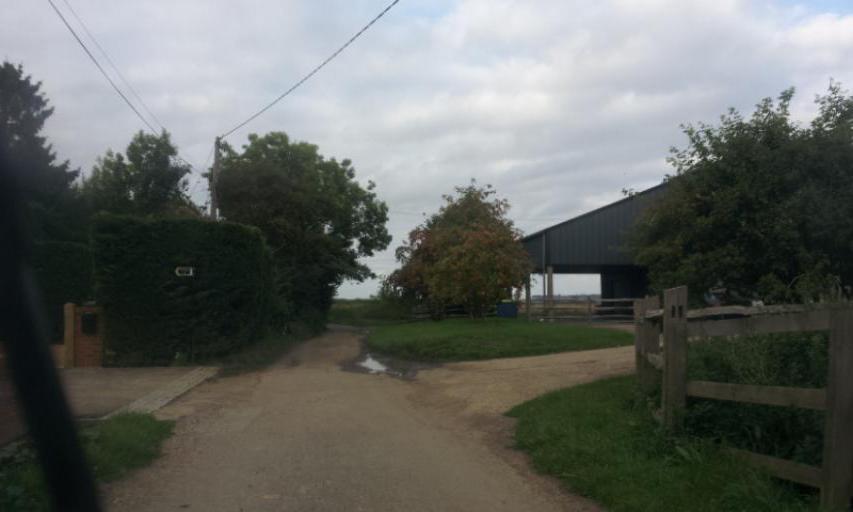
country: GB
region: England
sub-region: Kent
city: Hadlow
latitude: 51.2118
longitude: 0.3602
